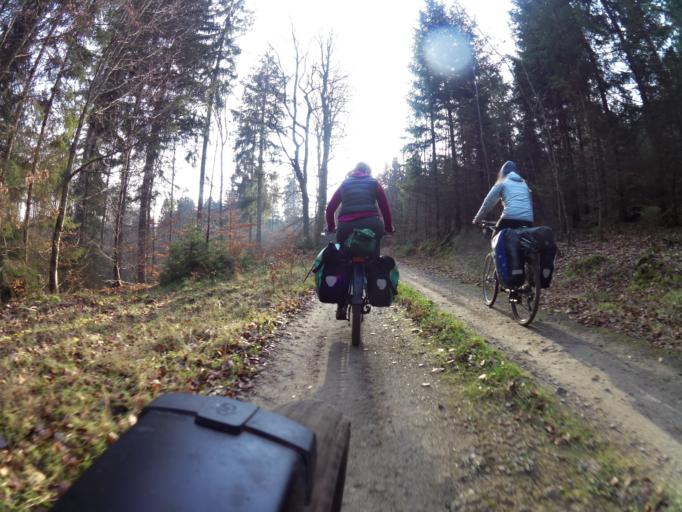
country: PL
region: West Pomeranian Voivodeship
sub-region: Powiat koszalinski
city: Polanow
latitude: 54.1742
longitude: 16.7259
